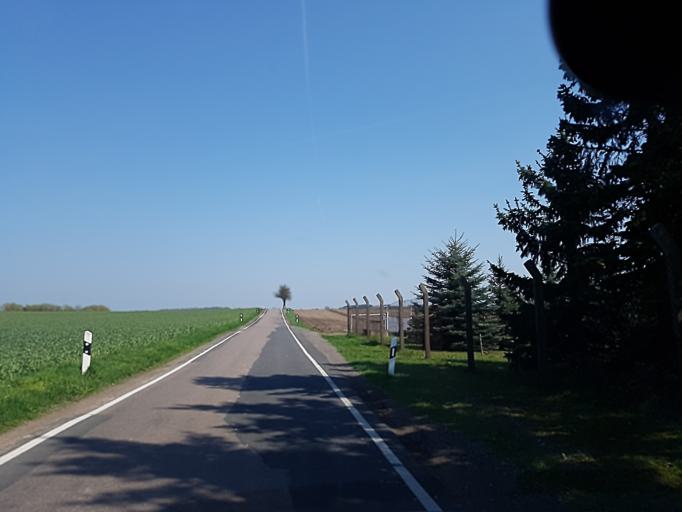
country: DE
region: Saxony
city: Cavertitz
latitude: 51.3886
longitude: 13.1366
